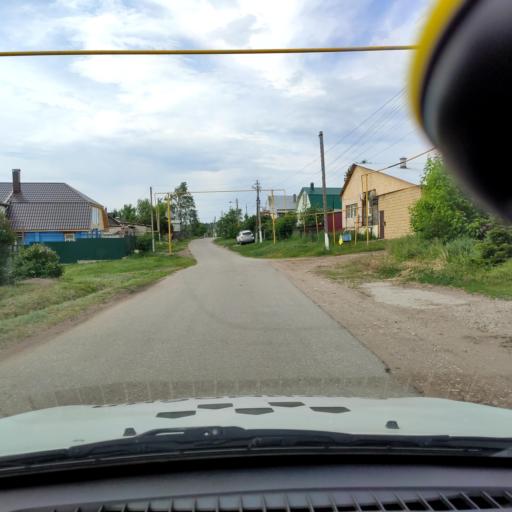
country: RU
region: Samara
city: Zhigulevsk
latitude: 53.5474
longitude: 49.5288
